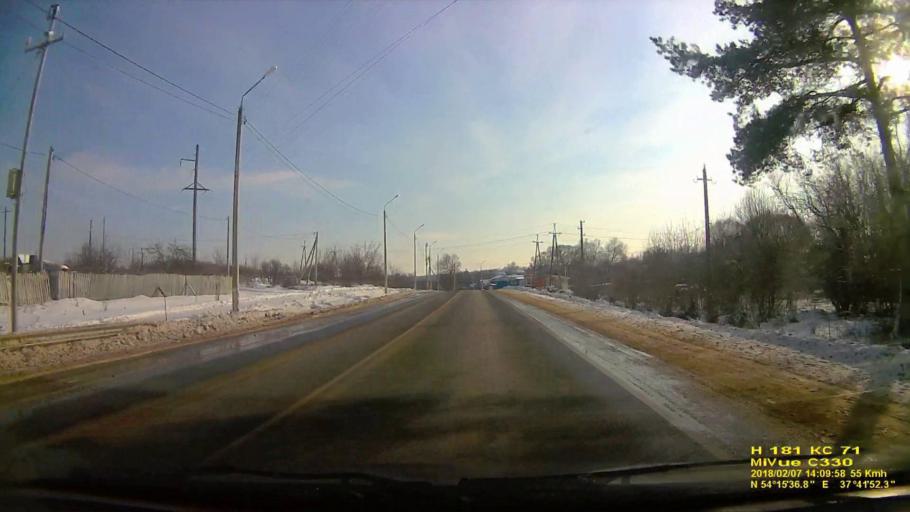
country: RU
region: Tula
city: Gorelki
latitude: 54.2602
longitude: 37.6978
